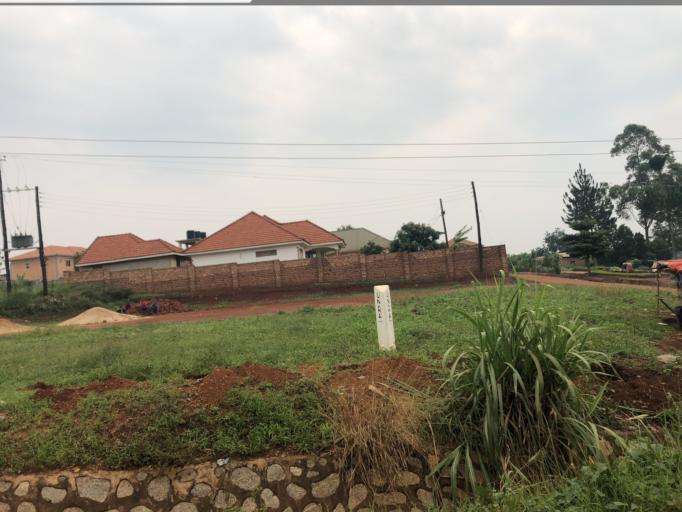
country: UG
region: Central Region
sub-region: Mukono District
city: Mukono
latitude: 0.3455
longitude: 32.7641
